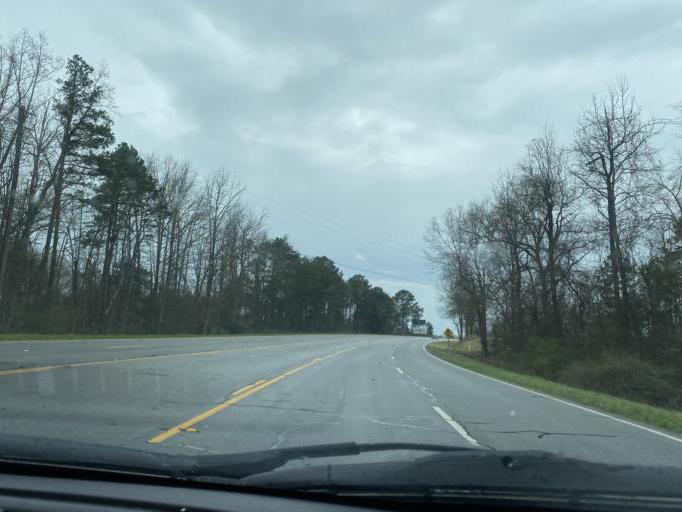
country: US
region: South Carolina
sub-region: Cherokee County
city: Gaffney
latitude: 35.0552
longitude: -81.6813
